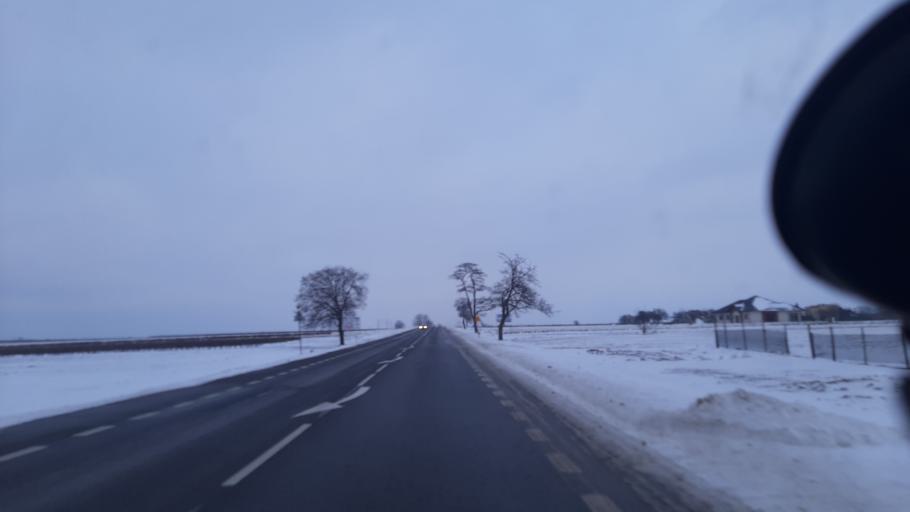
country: PL
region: Lublin Voivodeship
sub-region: Powiat pulawski
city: Markuszow
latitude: 51.3817
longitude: 22.2296
